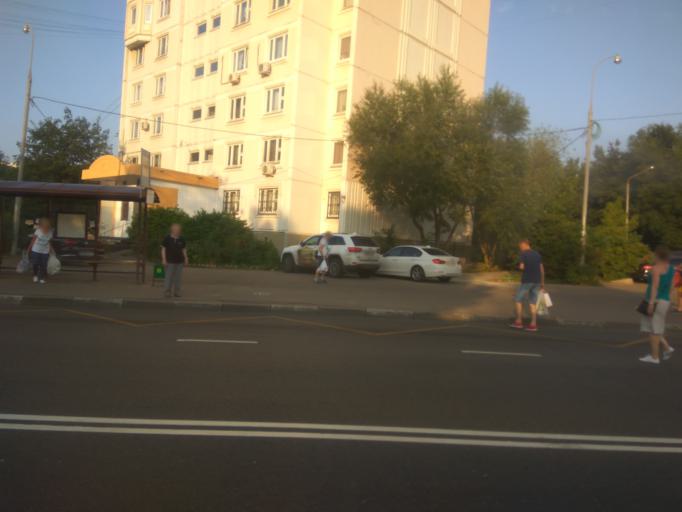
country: RU
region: Moscow
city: Orekhovo-Borisovo
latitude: 55.6145
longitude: 37.7067
